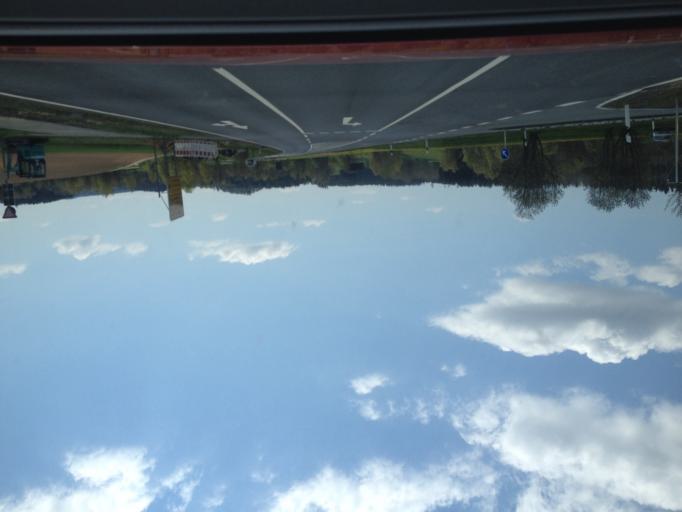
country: DE
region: Bavaria
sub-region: Upper Franconia
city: Marktredwitz
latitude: 49.9758
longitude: 12.0935
